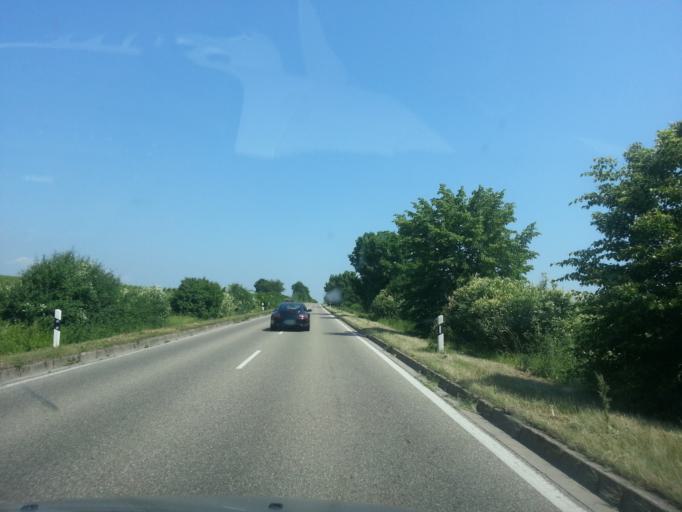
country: DE
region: Rheinland-Pfalz
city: Kallstadt
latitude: 49.4843
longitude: 8.1890
